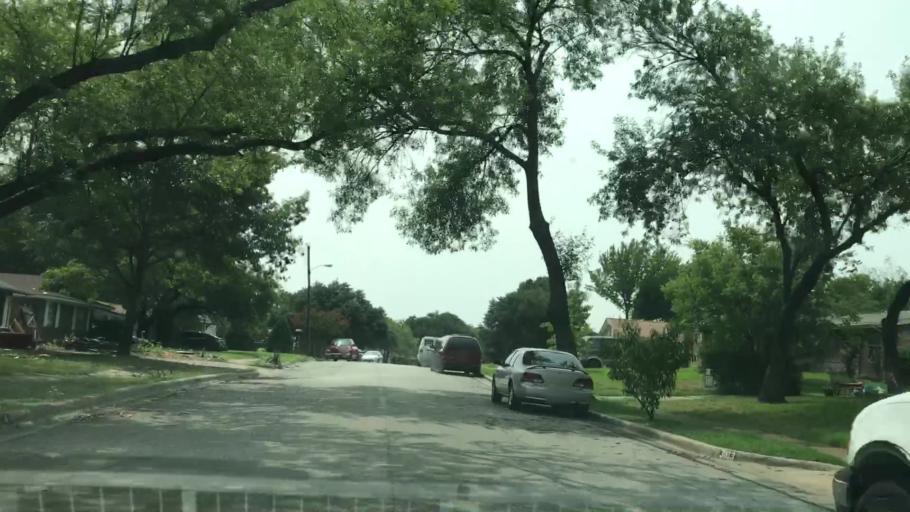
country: US
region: Texas
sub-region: Dallas County
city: Irving
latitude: 32.8398
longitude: -97.0023
